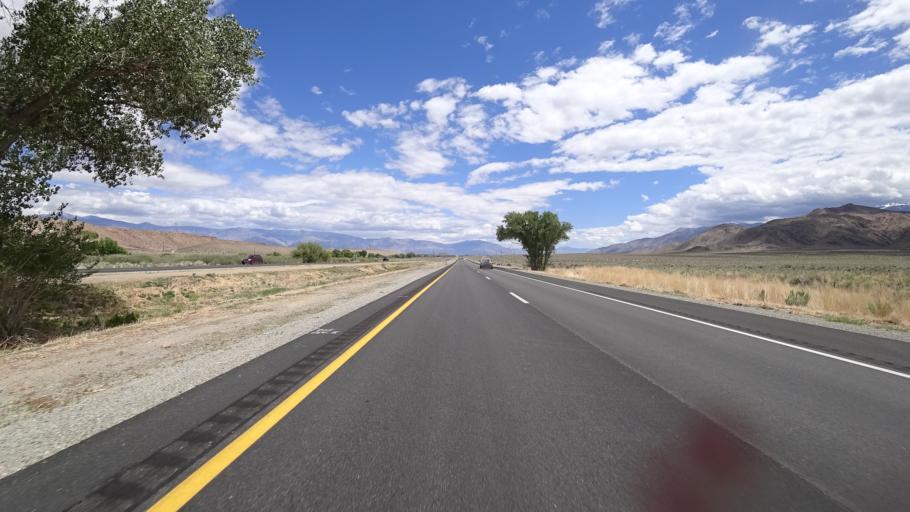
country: US
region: California
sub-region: Inyo County
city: West Bishop
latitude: 37.4029
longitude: -118.5362
